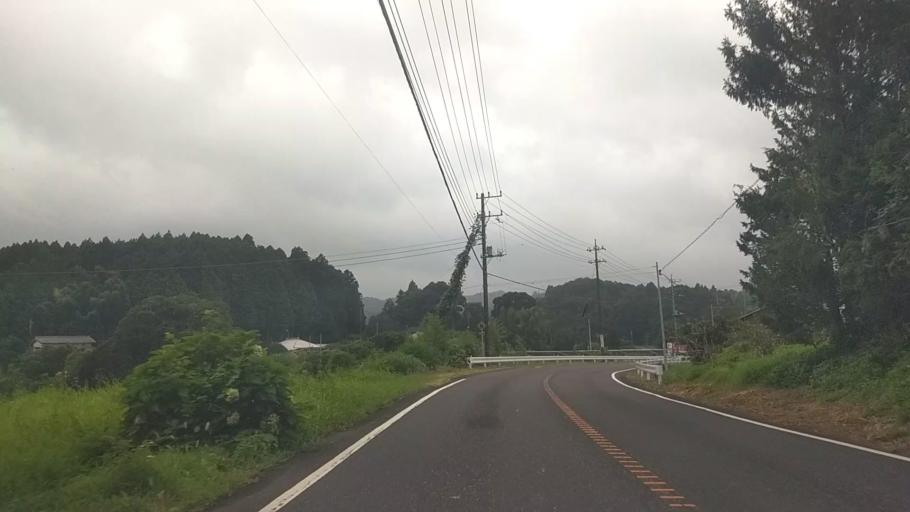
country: JP
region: Chiba
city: Kawaguchi
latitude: 35.2305
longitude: 140.0751
